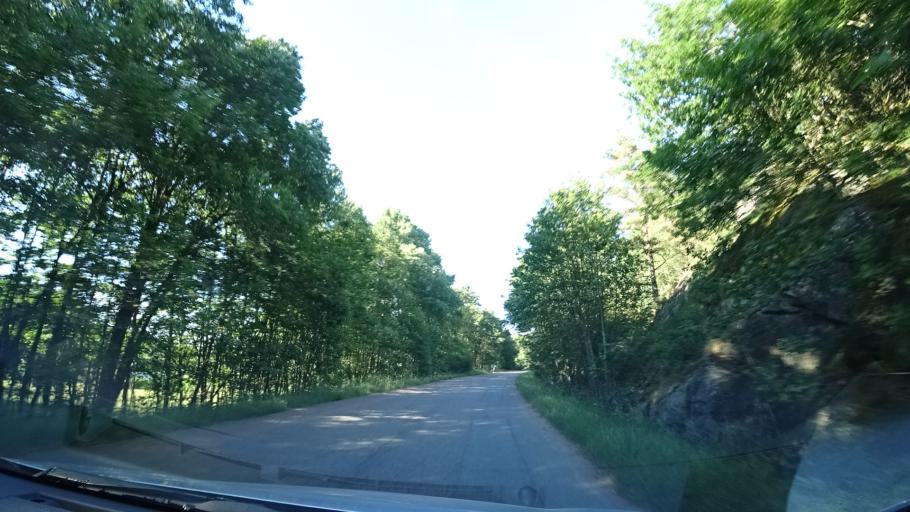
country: SE
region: Vaestra Goetaland
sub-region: Goteborg
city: Billdal
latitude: 57.5750
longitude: 11.9766
